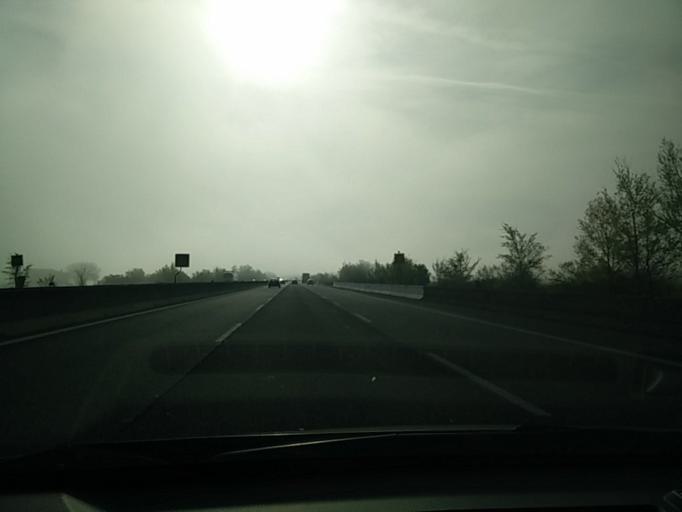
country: IT
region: Emilia-Romagna
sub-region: Provincia di Bologna
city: Osteria Grande
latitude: 44.4558
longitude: 11.5254
